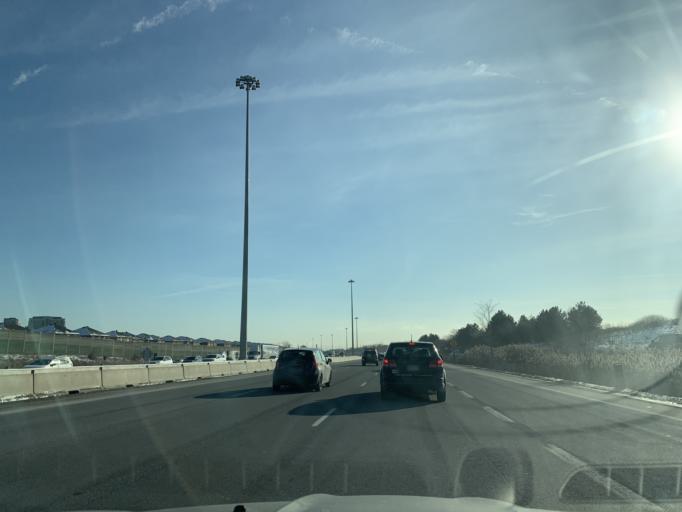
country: CA
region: Ontario
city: Etobicoke
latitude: 43.7328
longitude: -79.6273
